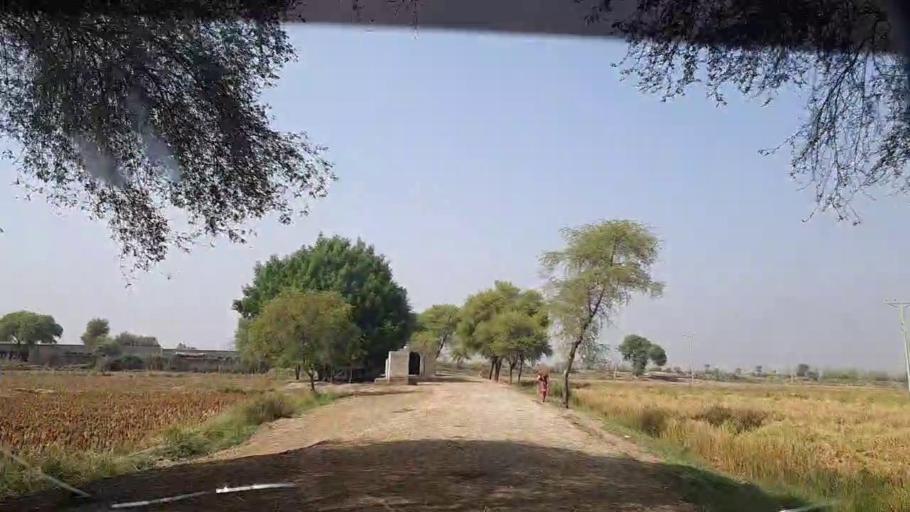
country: PK
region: Sindh
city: Shikarpur
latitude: 28.1161
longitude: 68.6567
